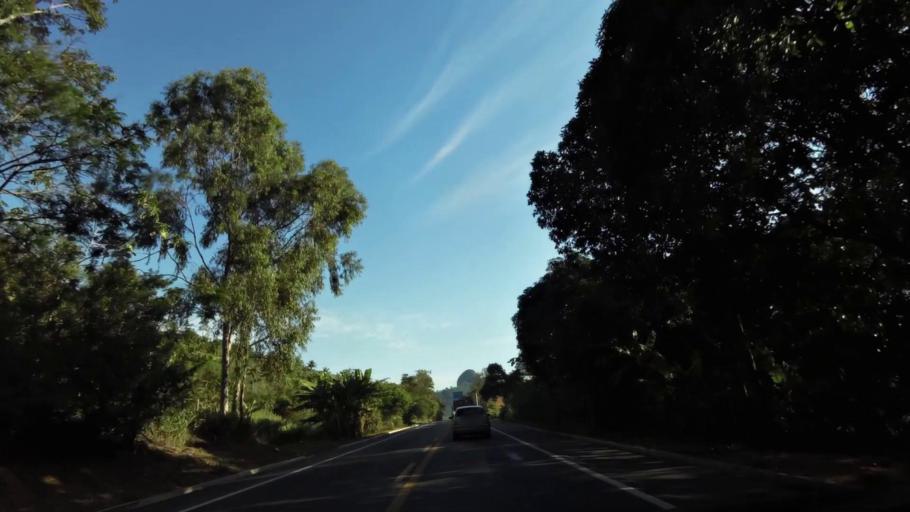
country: BR
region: Espirito Santo
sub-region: Guarapari
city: Guarapari
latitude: -20.5409
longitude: -40.4820
